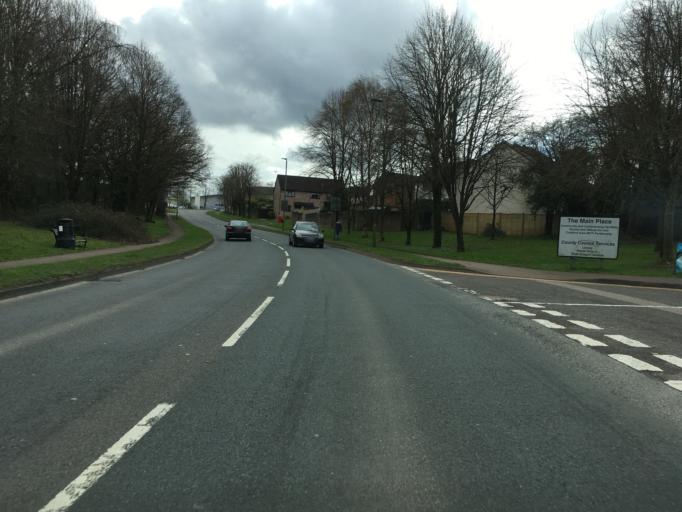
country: GB
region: England
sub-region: Gloucestershire
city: Coleford
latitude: 51.7910
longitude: -2.6144
